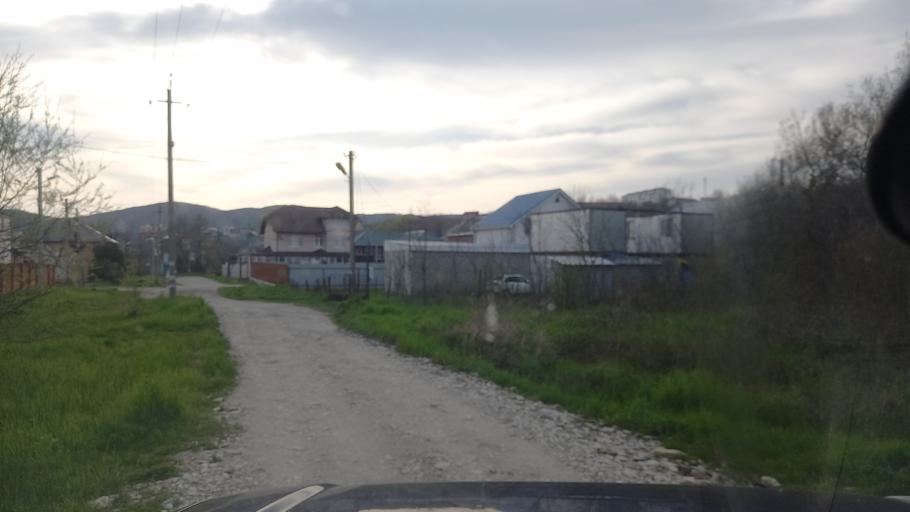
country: RU
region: Krasnodarskiy
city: Arkhipo-Osipovka
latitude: 44.3681
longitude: 38.5473
